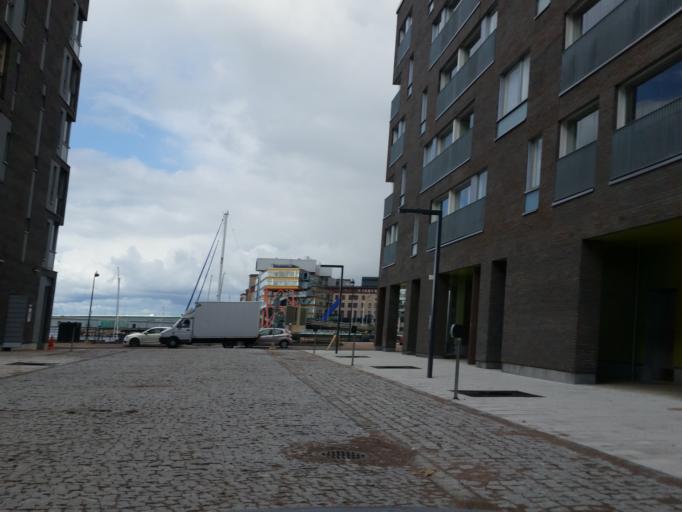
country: FI
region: Uusimaa
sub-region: Helsinki
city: Helsinki
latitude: 60.1584
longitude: 24.9070
